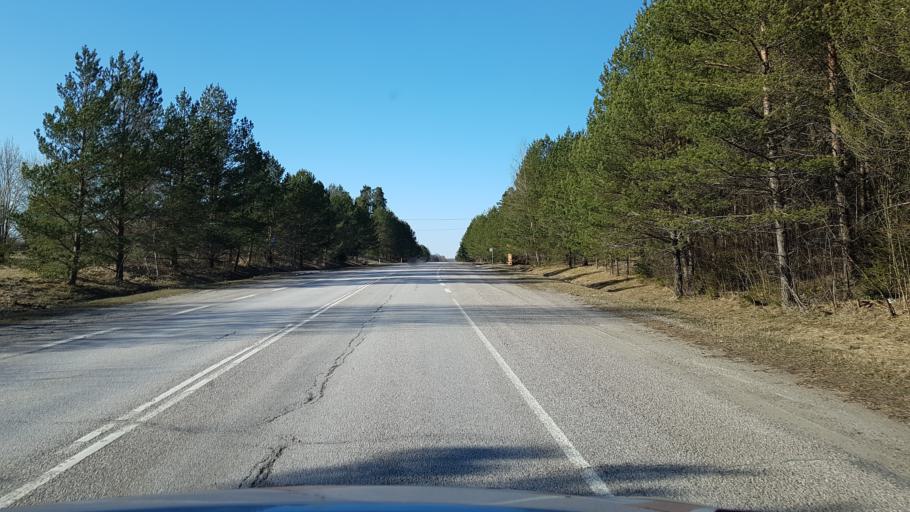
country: EE
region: Ida-Virumaa
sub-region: Johvi vald
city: Johvi
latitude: 59.1635
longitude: 27.3532
